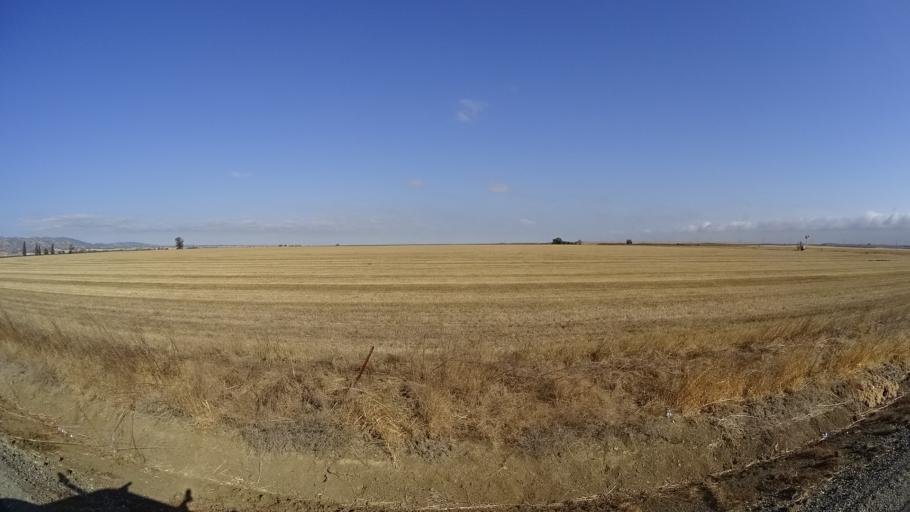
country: US
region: California
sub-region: Yolo County
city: Esparto
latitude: 38.7810
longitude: -122.0372
